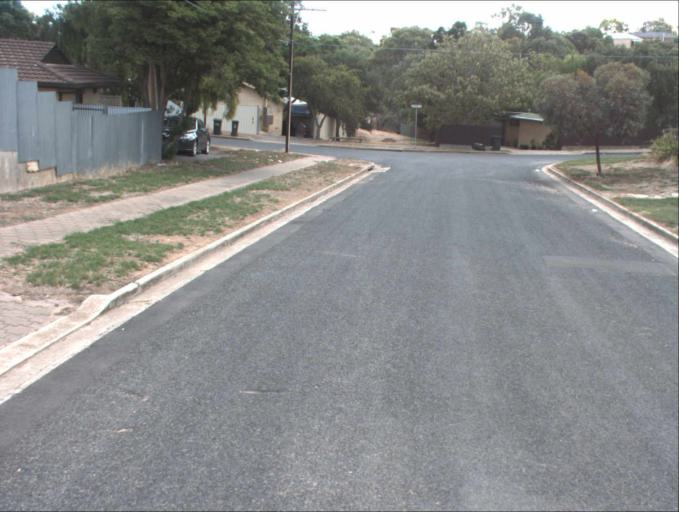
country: AU
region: South Australia
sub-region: Port Adelaide Enfield
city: Gilles Plains
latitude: -34.8422
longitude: 138.6502
